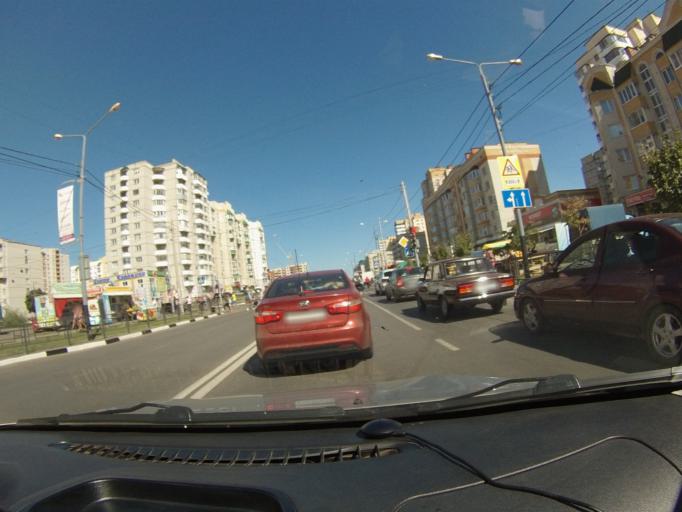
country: RU
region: Tambov
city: Tambov
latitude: 52.7680
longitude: 41.4034
